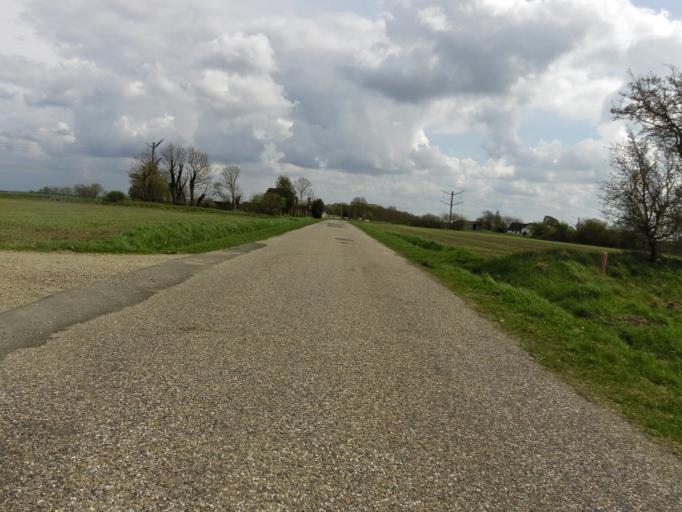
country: DK
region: South Denmark
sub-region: Tonder Kommune
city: Toftlund
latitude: 55.2101
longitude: 9.1456
